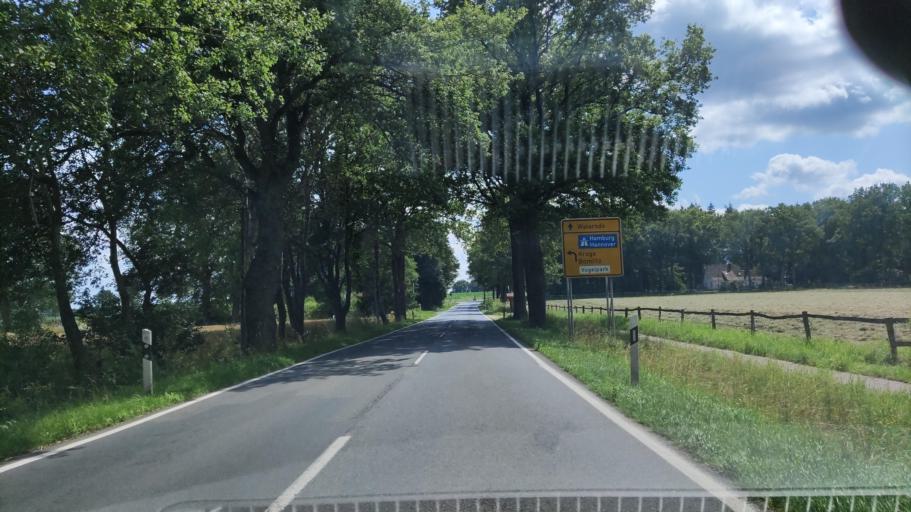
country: DE
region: Lower Saxony
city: Walsrode
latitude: 52.9104
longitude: 9.5749
